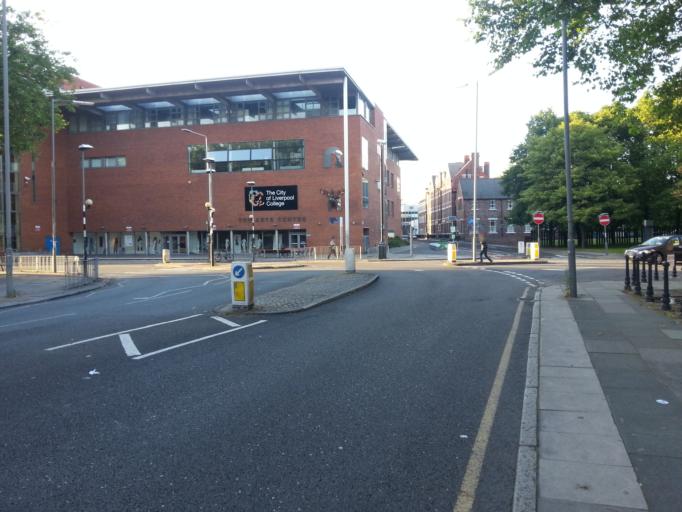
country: GB
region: England
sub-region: Liverpool
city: Liverpool
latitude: 53.4007
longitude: -2.9674
